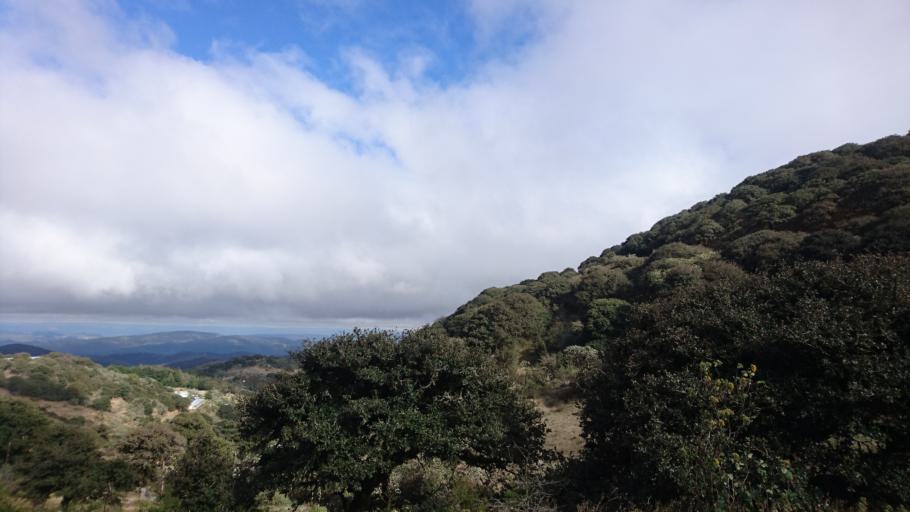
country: MX
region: San Luis Potosi
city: Zaragoza
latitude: 22.0697
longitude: -100.6417
